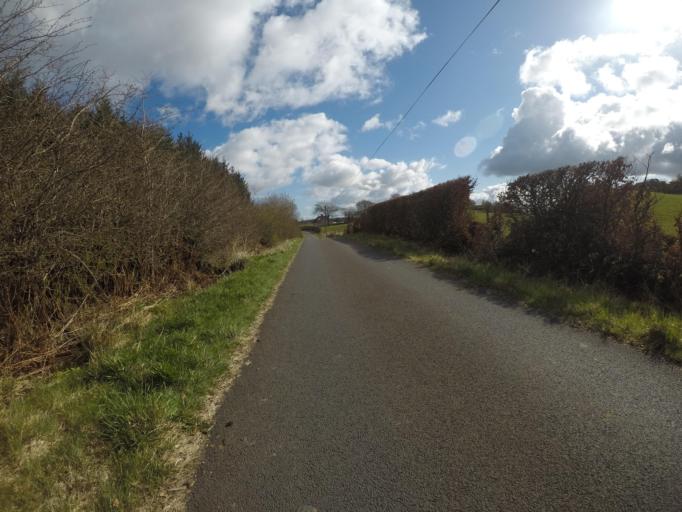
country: GB
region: Scotland
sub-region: North Ayrshire
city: Beith
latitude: 55.7081
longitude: -4.6596
